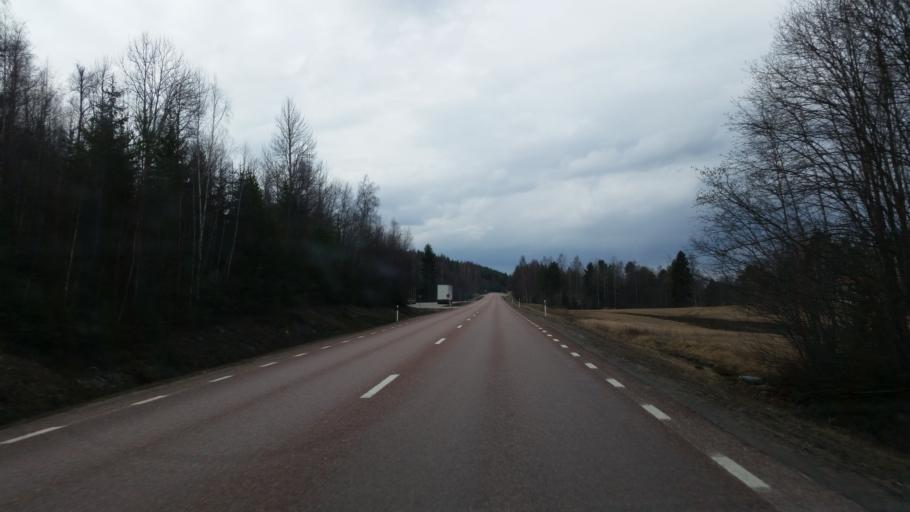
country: SE
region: Gaevleborg
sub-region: Ljusdals Kommun
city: Jaervsoe
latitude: 61.7319
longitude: 16.1647
